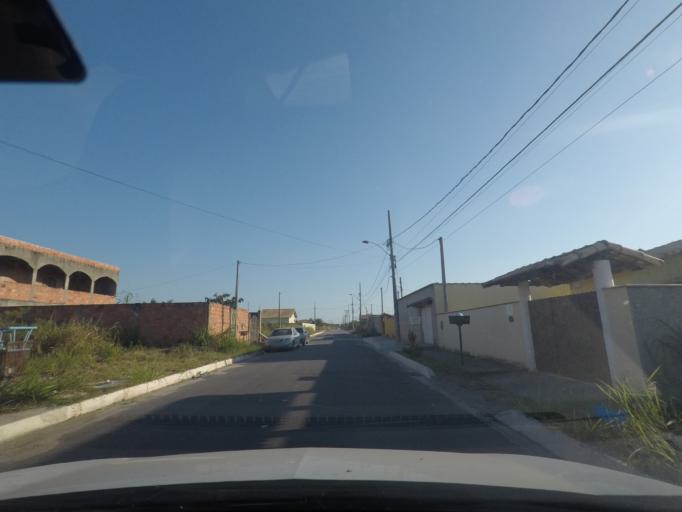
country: BR
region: Rio de Janeiro
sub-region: Marica
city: Marica
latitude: -22.9584
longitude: -42.9361
